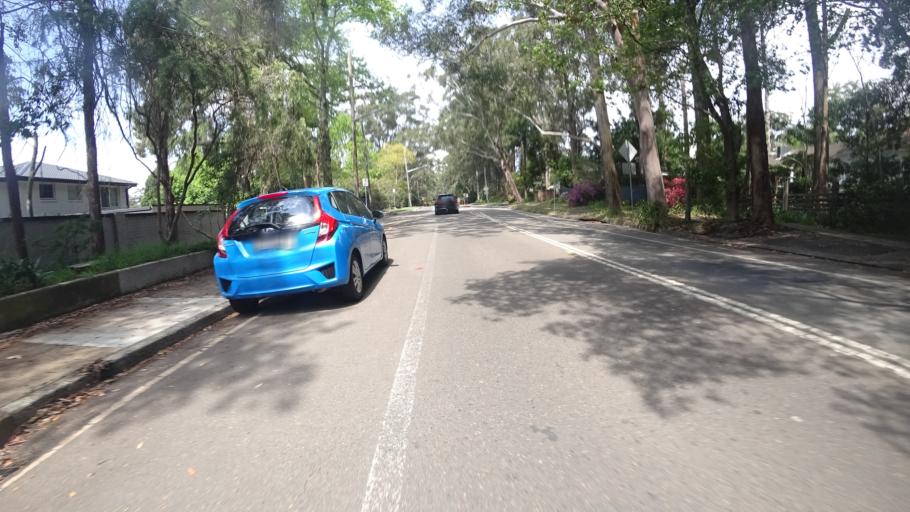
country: AU
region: New South Wales
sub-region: City of Sydney
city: North Turramurra
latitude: -33.7172
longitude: 151.1381
